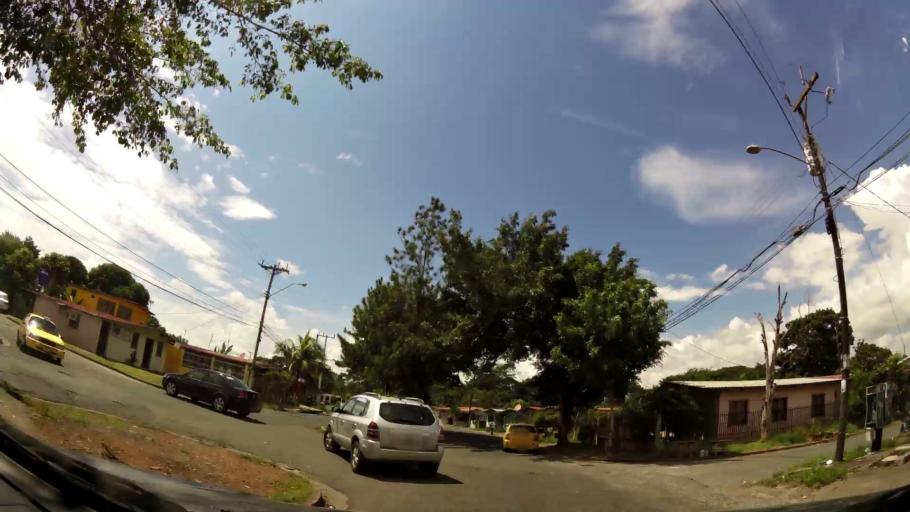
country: PA
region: Panama
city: Nuevo Arraijan
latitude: 8.9140
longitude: -79.7108
